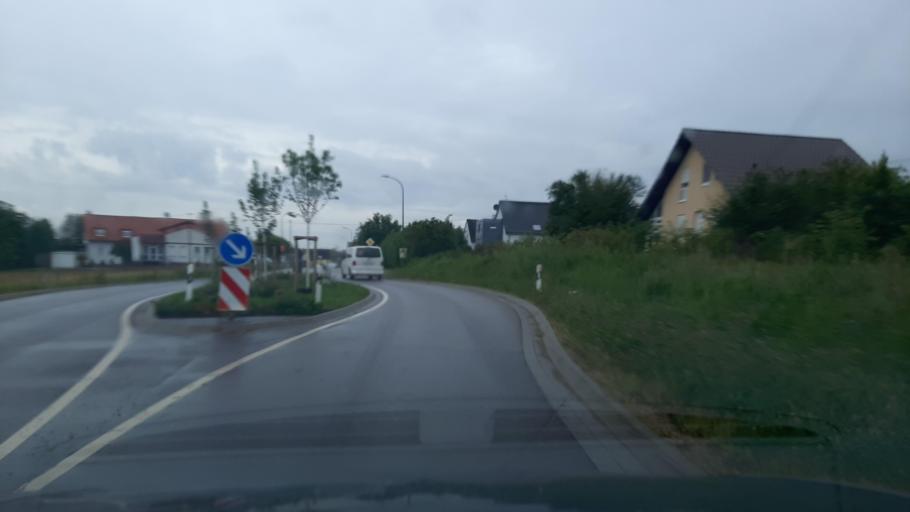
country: DE
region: Rheinland-Pfalz
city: Badem
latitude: 50.0075
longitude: 6.6093
